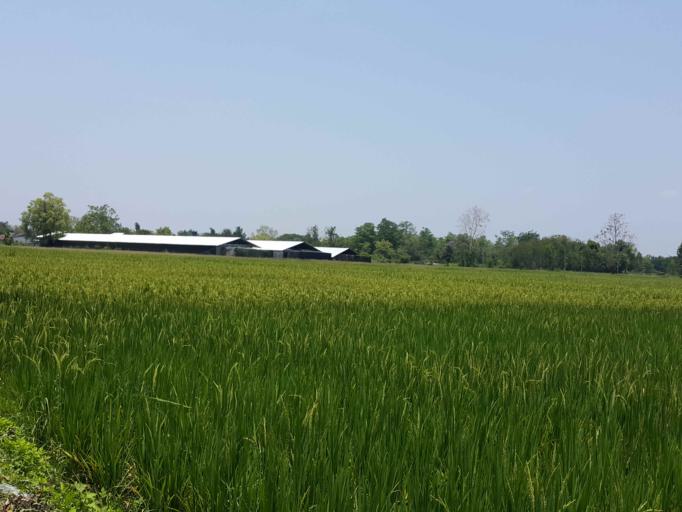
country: TH
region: Chiang Mai
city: San Kamphaeng
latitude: 18.8083
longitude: 99.1147
